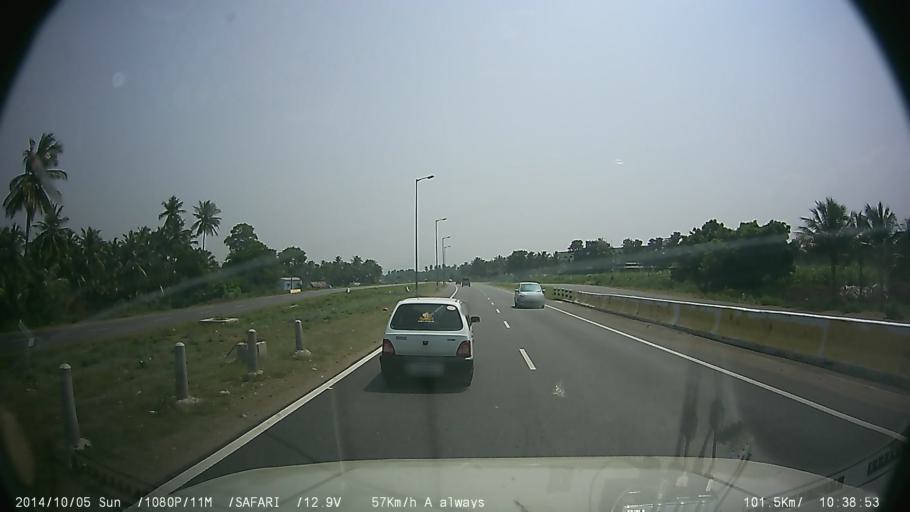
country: IN
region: Tamil Nadu
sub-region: Salem
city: Salem
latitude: 11.6641
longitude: 78.2467
